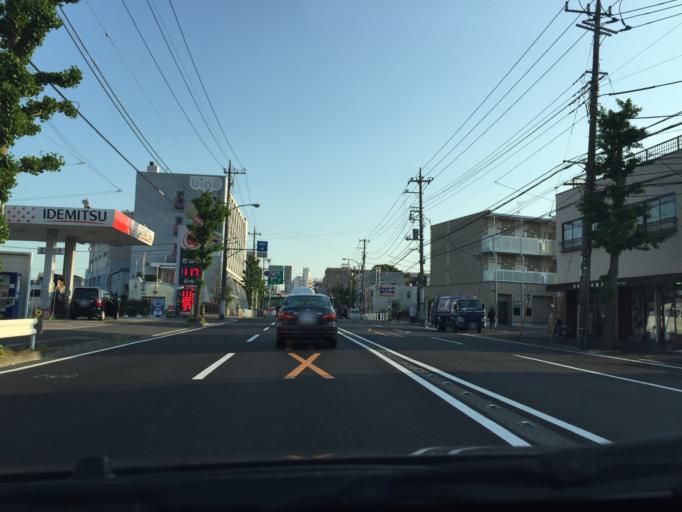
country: JP
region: Kanagawa
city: Yokohama
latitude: 35.4201
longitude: 139.6006
